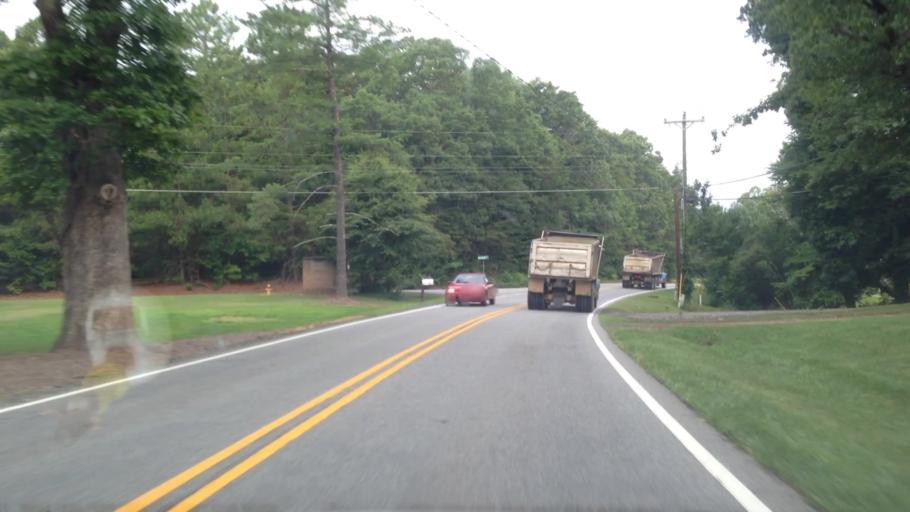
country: US
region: North Carolina
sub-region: Forsyth County
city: Walkertown
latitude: 36.1888
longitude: -80.2129
